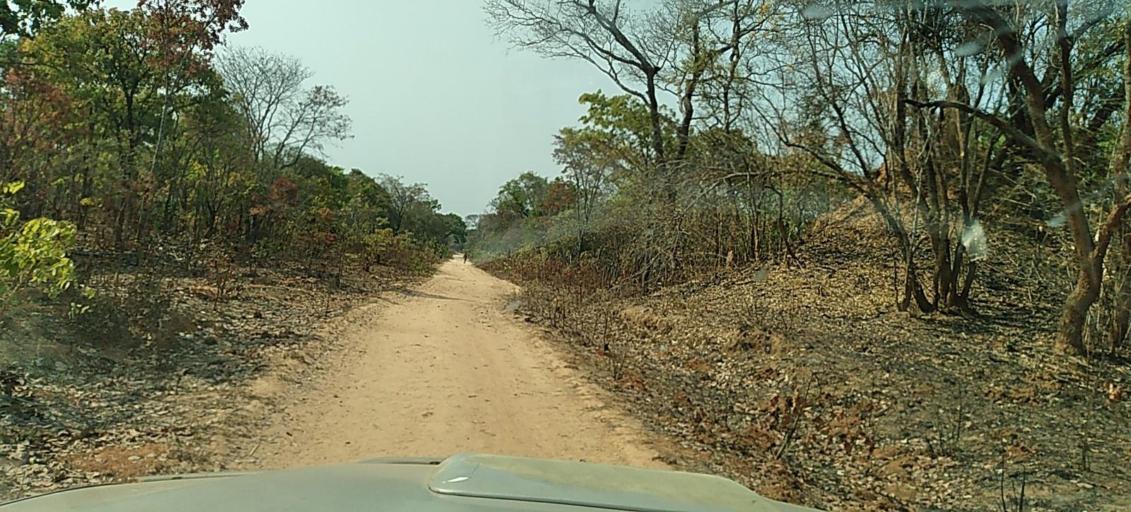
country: ZM
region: North-Western
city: Kasempa
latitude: -13.5455
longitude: 26.4087
